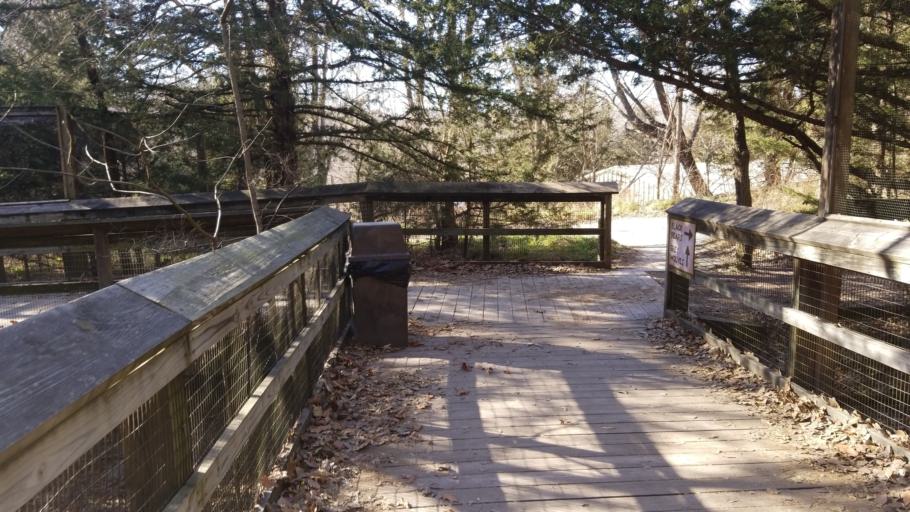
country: US
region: Nebraska
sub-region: Saunders County
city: Ashland
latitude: 41.0138
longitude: -96.2901
